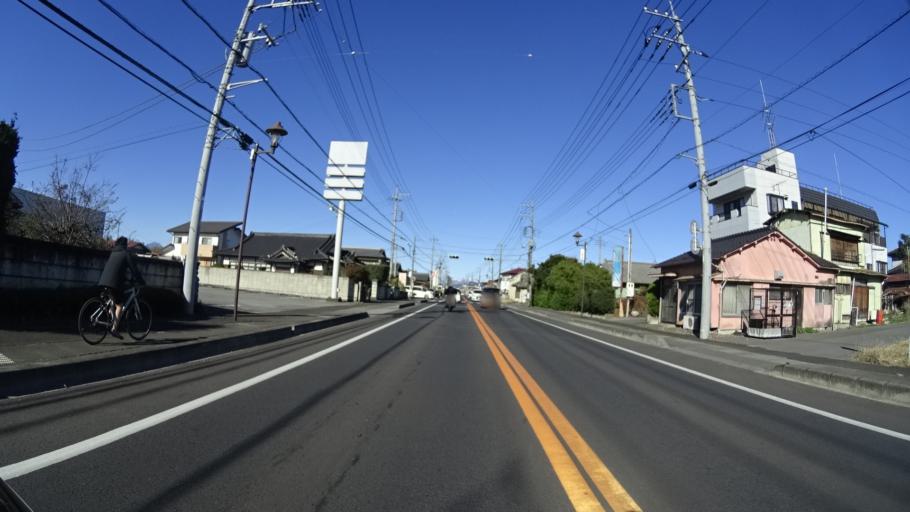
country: JP
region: Tochigi
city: Kanuma
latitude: 36.5093
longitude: 139.7515
